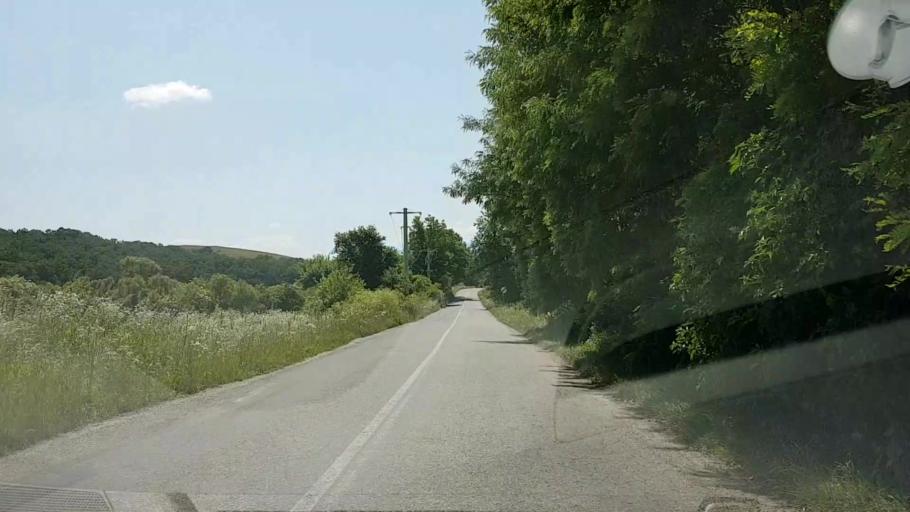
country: RO
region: Brasov
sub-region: Comuna Cincu
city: Cincu
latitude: 45.8685
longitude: 24.8232
